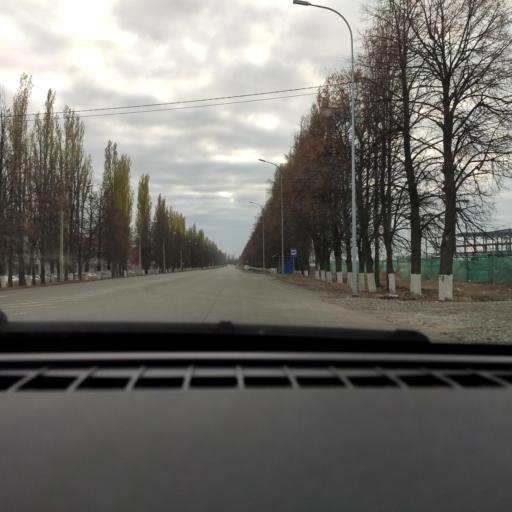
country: RU
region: Voronezj
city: Podgornoye
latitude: 51.8078
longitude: 39.2185
